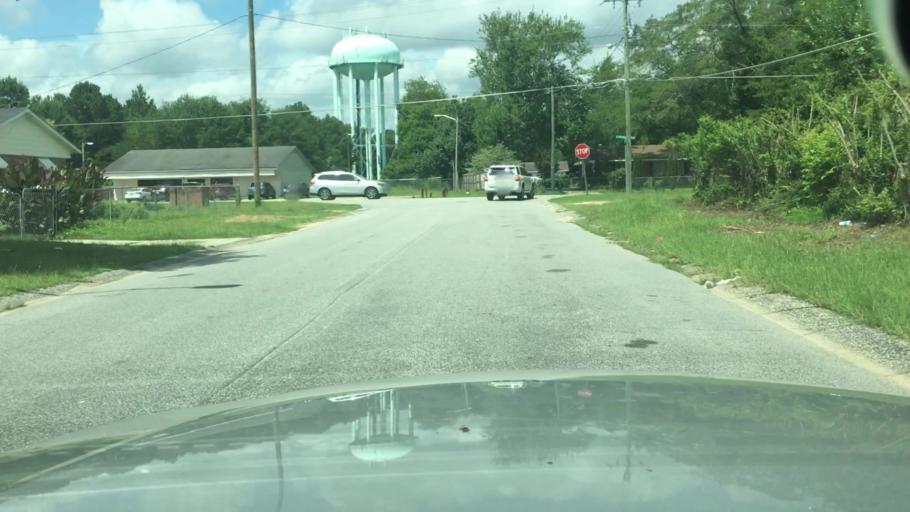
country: US
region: North Carolina
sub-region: Hoke County
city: Rockfish
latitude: 35.0331
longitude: -78.9969
